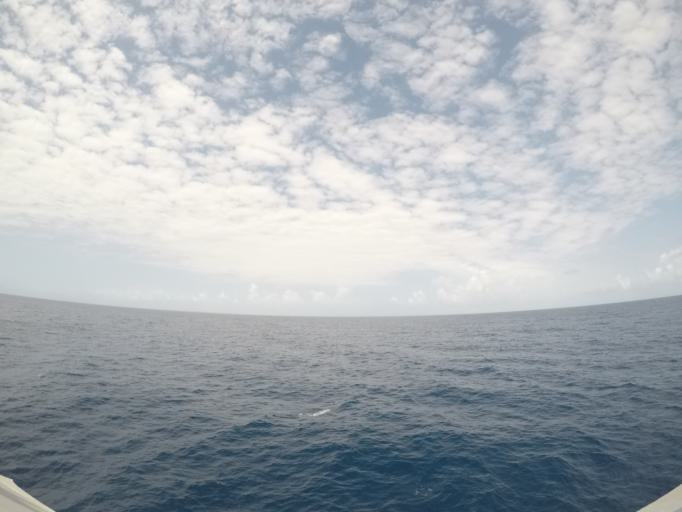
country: TZ
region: Zanzibar North
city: Nungwi
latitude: -5.5863
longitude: 39.3536
